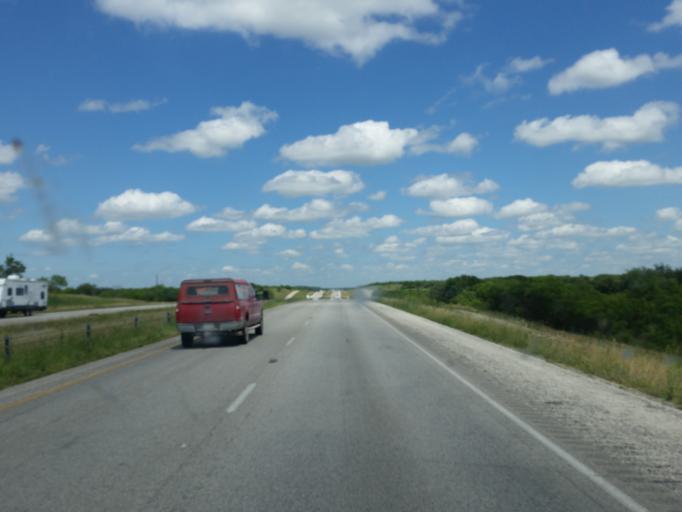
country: US
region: Texas
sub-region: Callahan County
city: Baird
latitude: 32.3825
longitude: -99.2788
